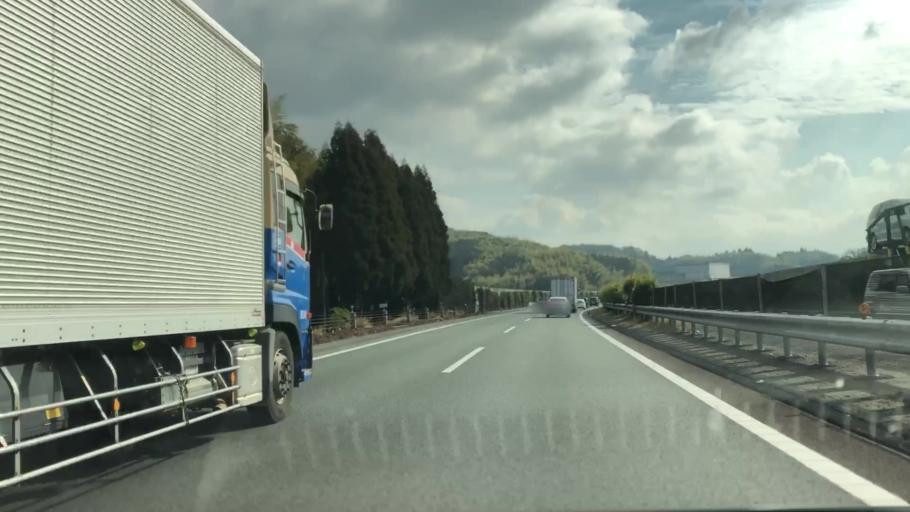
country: JP
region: Fukuoka
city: Setakamachi-takayanagi
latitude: 33.0870
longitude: 130.5406
